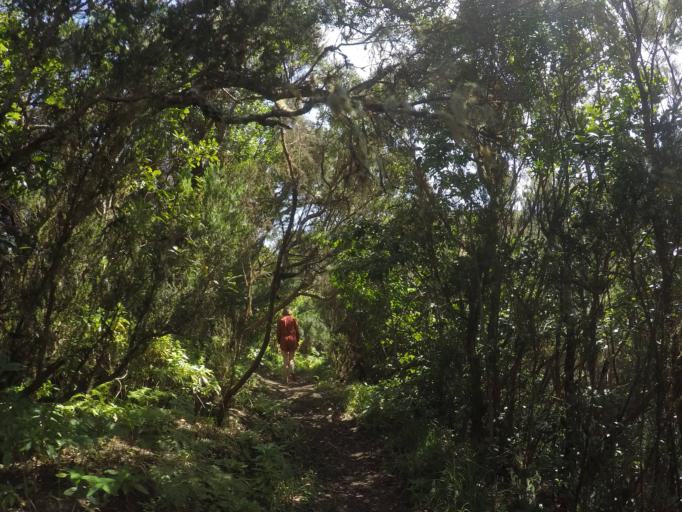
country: ES
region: Canary Islands
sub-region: Provincia de Santa Cruz de Tenerife
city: Santa Cruz de Tenerife
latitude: 28.5447
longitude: -16.2266
